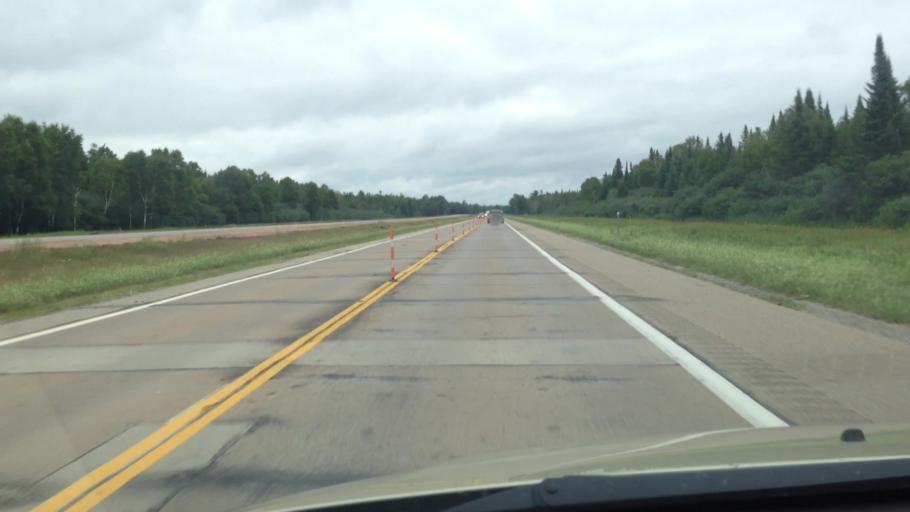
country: US
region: Michigan
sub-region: Delta County
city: Gladstone
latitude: 45.8780
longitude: -87.0147
